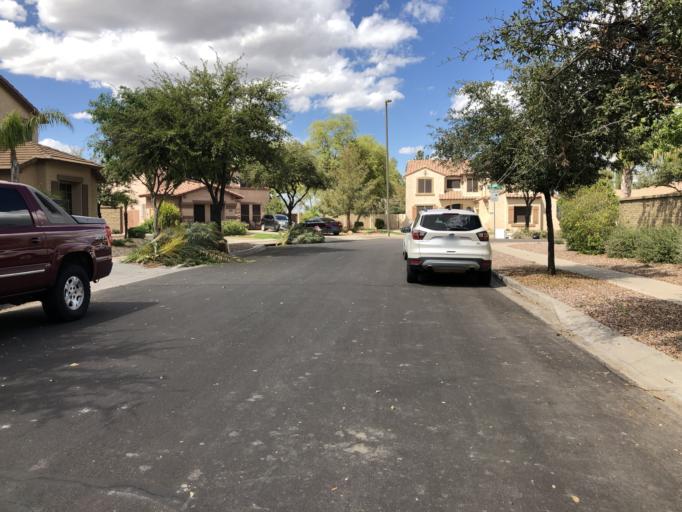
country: US
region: Arizona
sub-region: Maricopa County
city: Queen Creek
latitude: 33.2702
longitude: -111.6919
